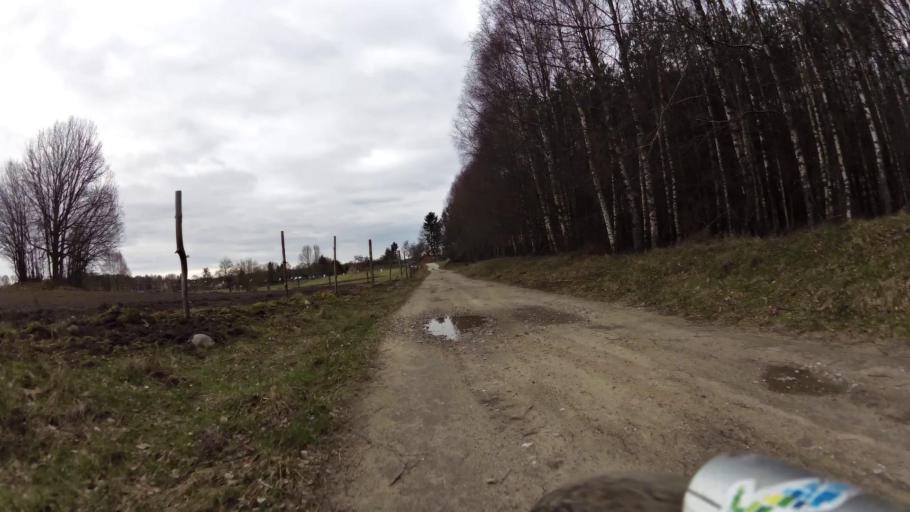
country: PL
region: Pomeranian Voivodeship
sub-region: Powiat bytowski
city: Trzebielino
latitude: 54.1094
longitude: 17.1303
